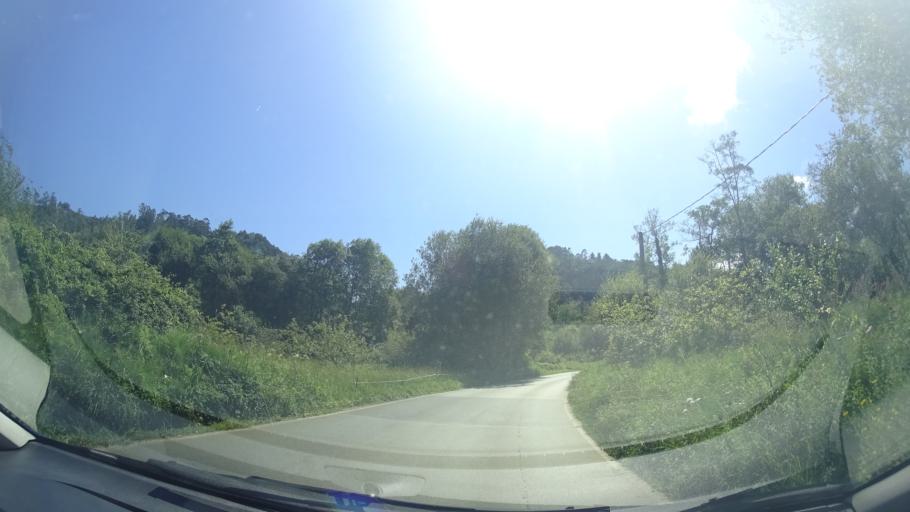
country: ES
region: Asturias
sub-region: Province of Asturias
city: Ribadesella
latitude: 43.4762
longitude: -5.1327
